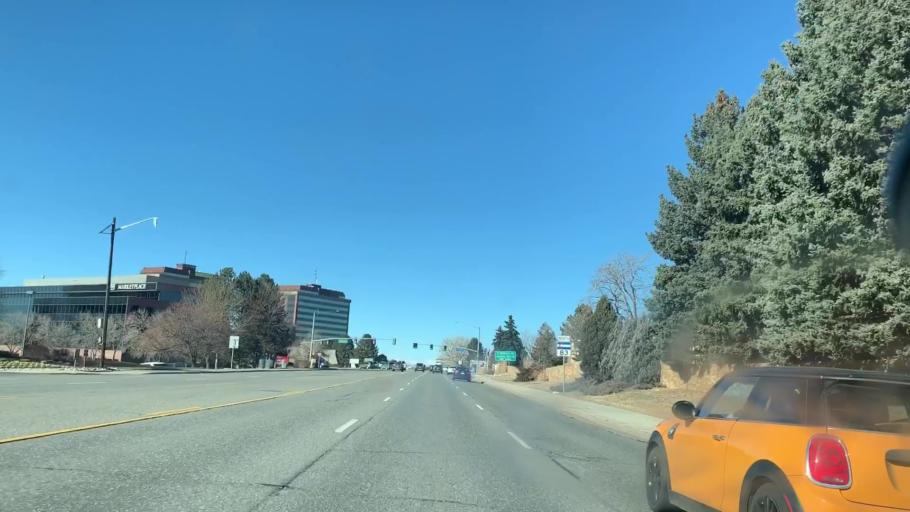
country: US
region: Colorado
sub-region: Adams County
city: Aurora
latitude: 39.6620
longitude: -104.8569
